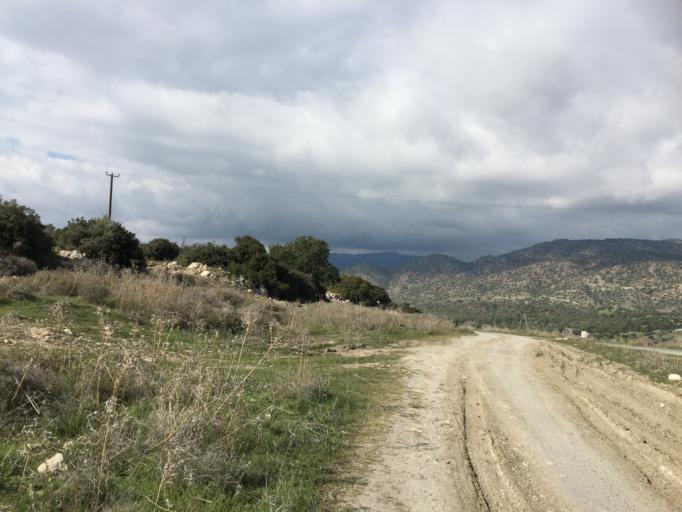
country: CY
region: Larnaka
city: Agios Tychon
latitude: 34.7450
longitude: 33.1369
